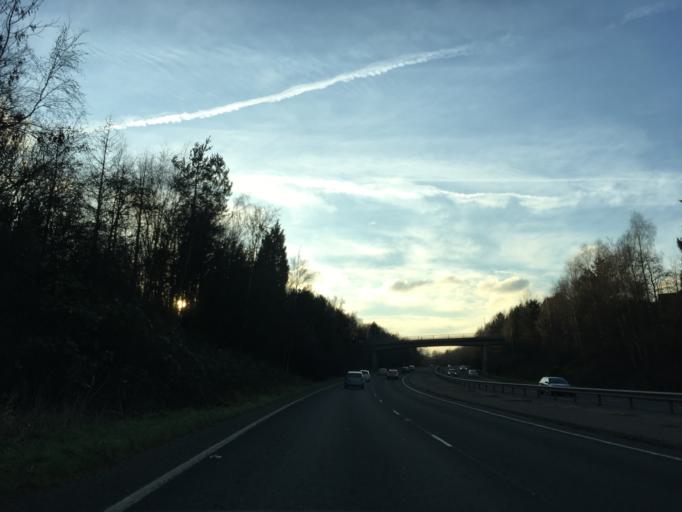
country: GB
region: England
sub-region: Cheshire East
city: Wilmslow
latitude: 53.3397
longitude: -2.2028
